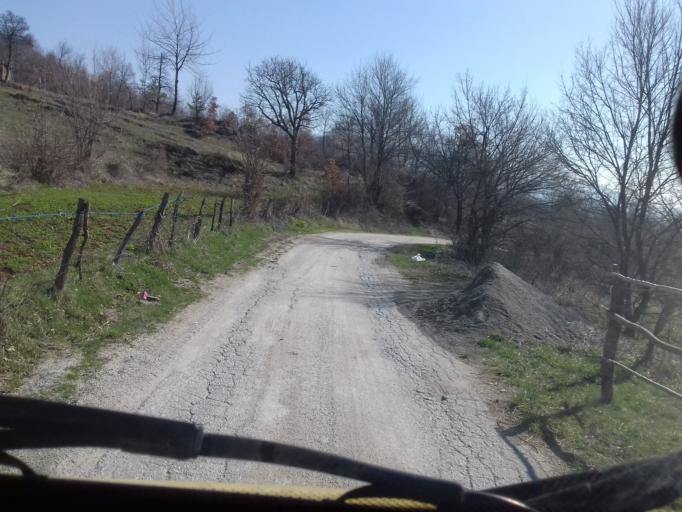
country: BA
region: Federation of Bosnia and Herzegovina
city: Travnik
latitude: 44.2478
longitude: 17.7257
